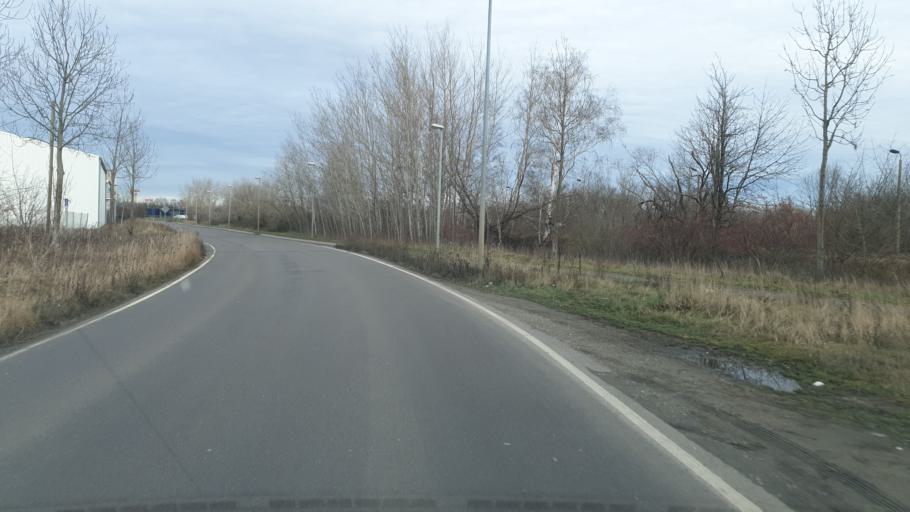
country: DE
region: Saxony
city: Kitzen
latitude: 51.2479
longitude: 12.2731
